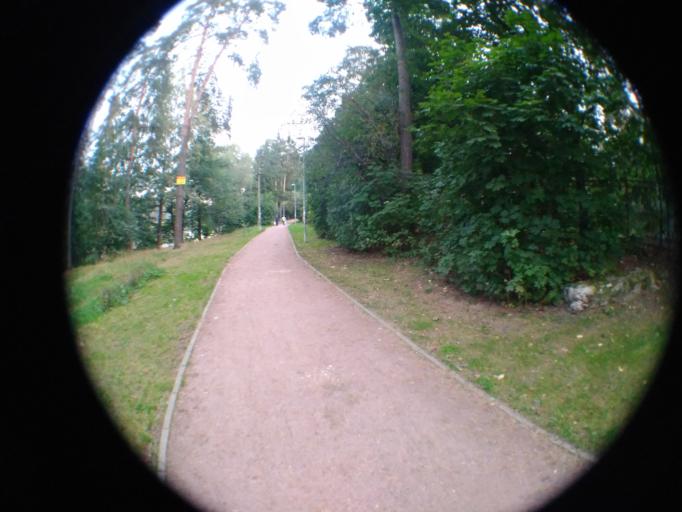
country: RU
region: Moskovskaya
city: Kratovo
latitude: 55.5890
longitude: 38.1571
